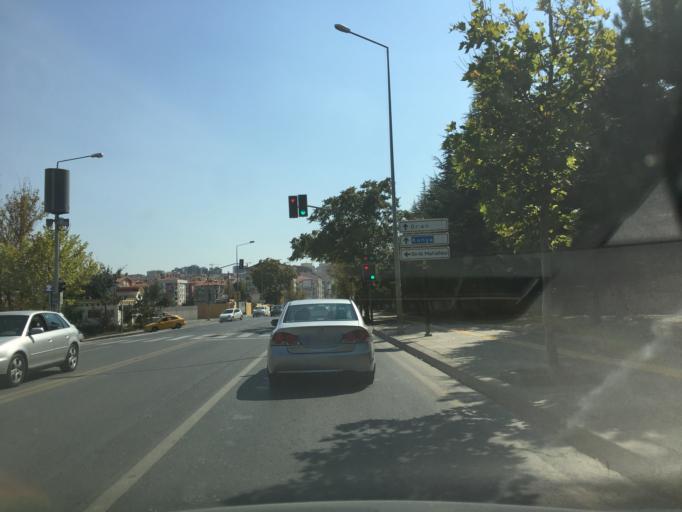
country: TR
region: Ankara
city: Cankaya
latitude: 39.8799
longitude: 32.8657
